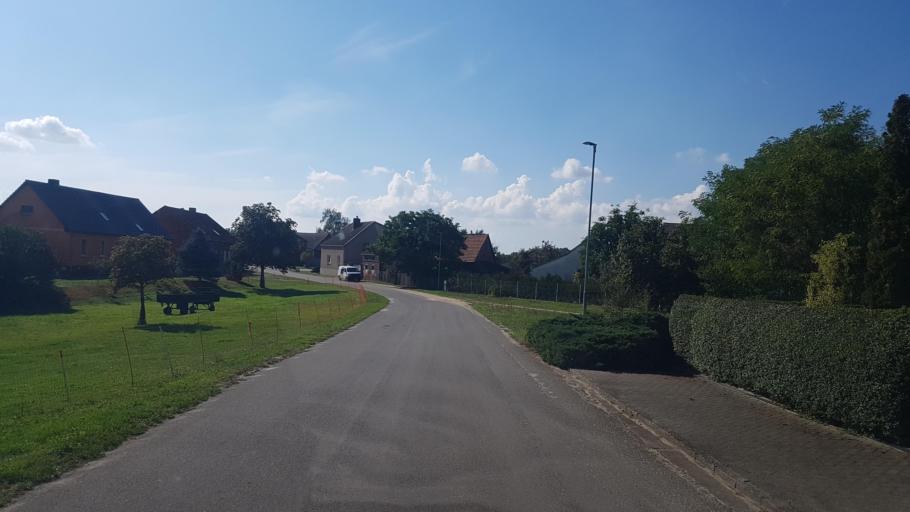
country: DE
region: Brandenburg
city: Ihlow
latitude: 51.8356
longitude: 13.3490
